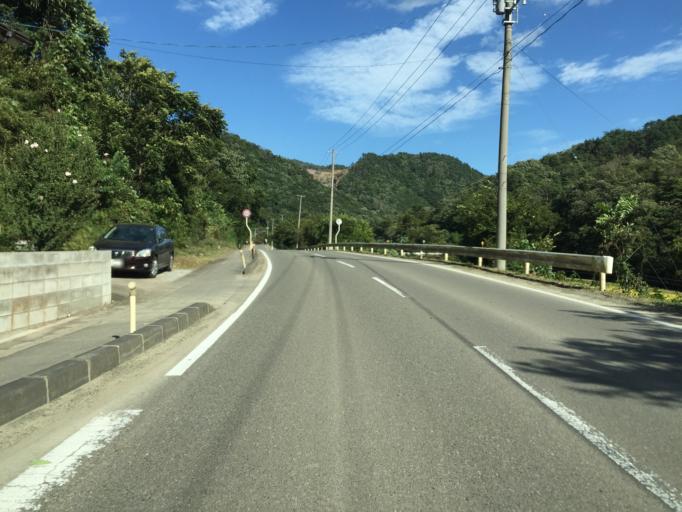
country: JP
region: Fukushima
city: Yanagawamachi-saiwaicho
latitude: 37.8551
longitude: 140.6349
